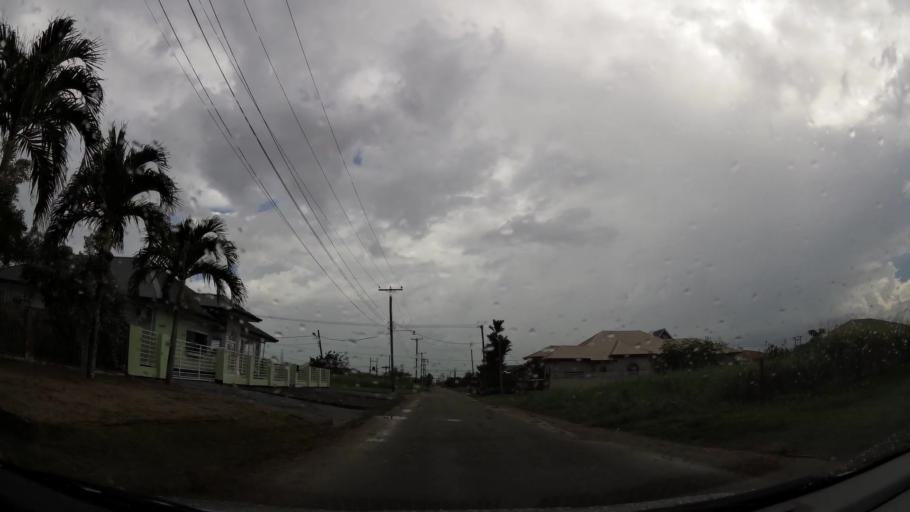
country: SR
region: Commewijne
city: Nieuw Amsterdam
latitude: 5.8607
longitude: -55.1157
